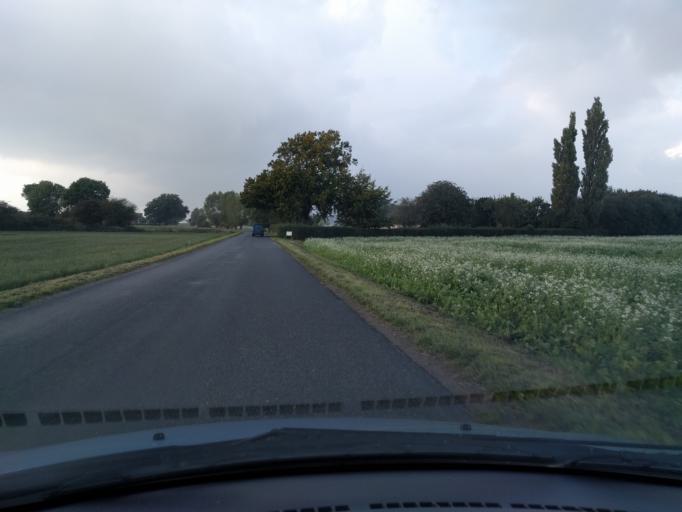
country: DK
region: South Denmark
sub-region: Kerteminde Kommune
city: Kerteminde
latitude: 55.4329
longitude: 10.6121
